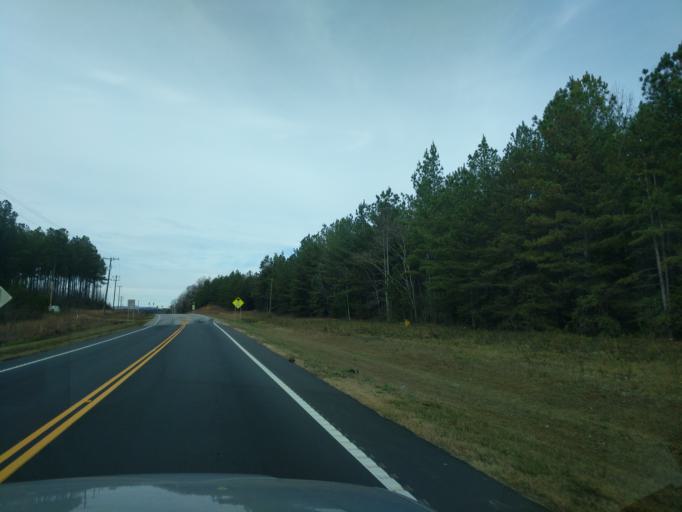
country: US
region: South Carolina
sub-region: Oconee County
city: Walhalla
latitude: 34.8119
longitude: -83.0355
